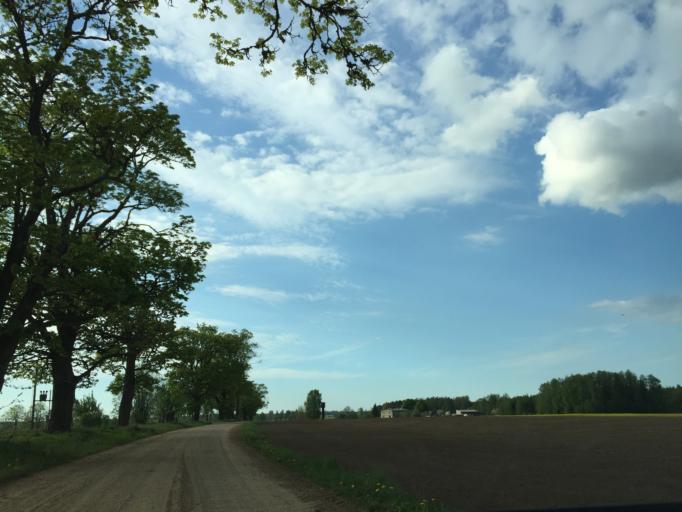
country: LV
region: Limbazu Rajons
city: Limbazi
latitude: 57.3490
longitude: 24.7041
